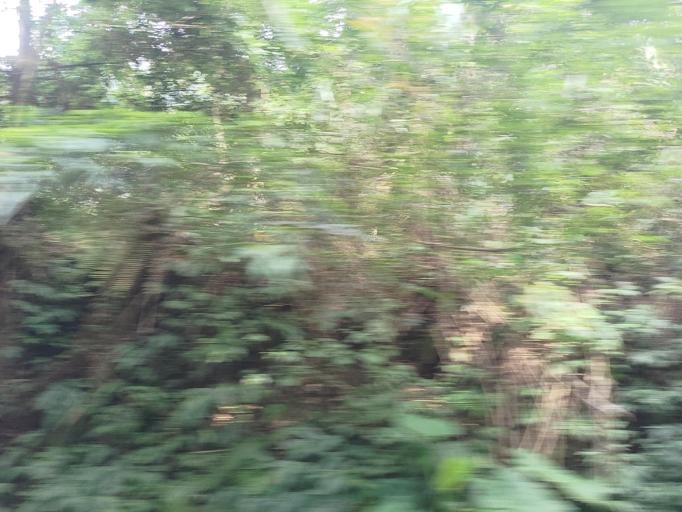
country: TW
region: Taiwan
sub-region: Hsinchu
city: Hsinchu
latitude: 24.6269
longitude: 121.0793
